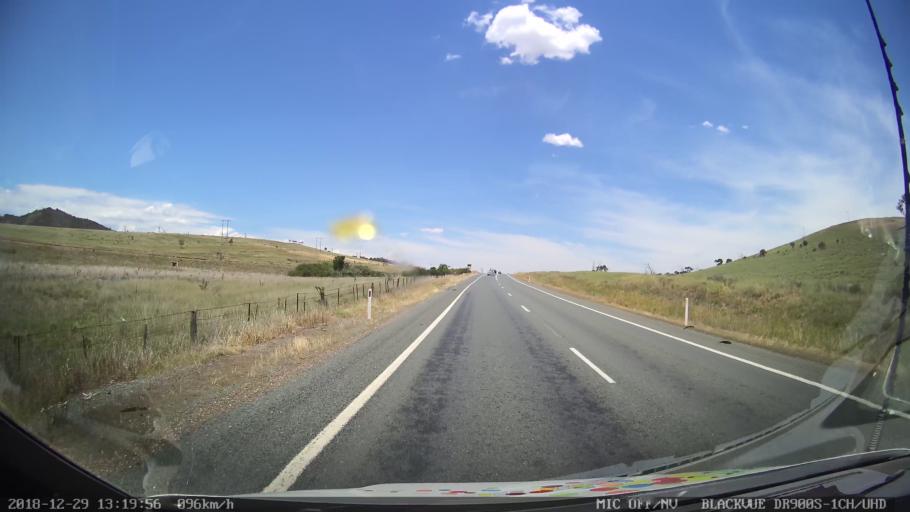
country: AU
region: Australian Capital Territory
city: Macarthur
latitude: -35.7724
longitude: 149.1619
